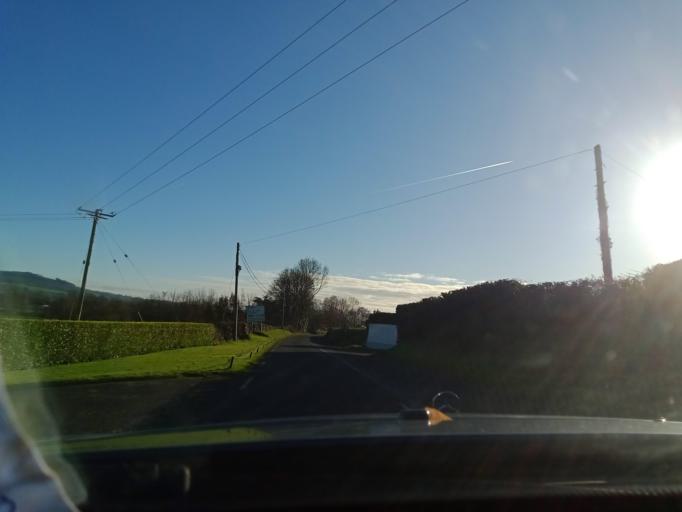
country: IE
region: Leinster
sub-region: Kilkenny
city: Piltown
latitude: 52.3735
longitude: -7.3387
